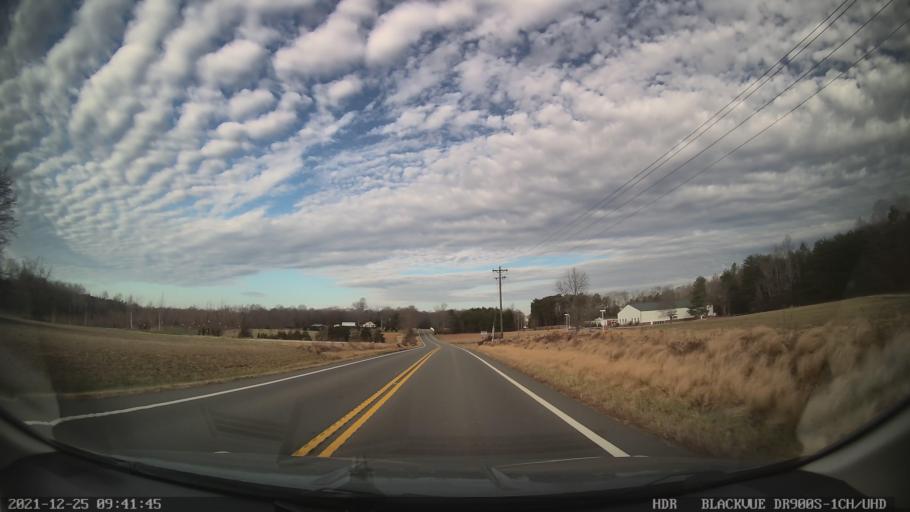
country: US
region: Virginia
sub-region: Goochland County
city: Goochland
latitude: 37.8189
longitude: -77.8807
